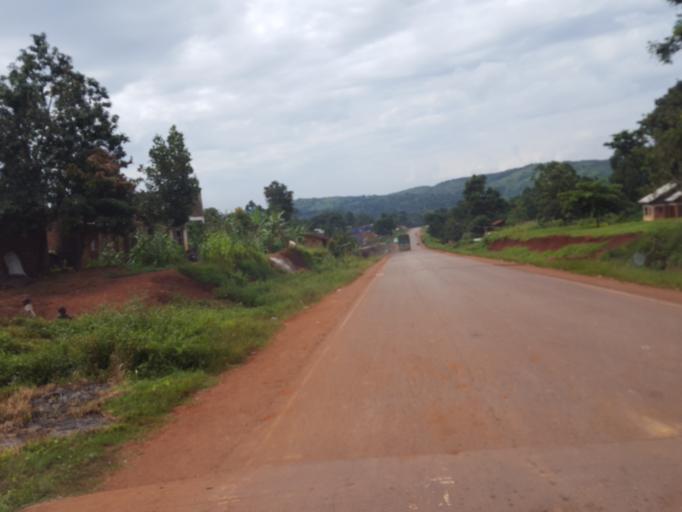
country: UG
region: Central Region
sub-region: Mityana District
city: Mityana
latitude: 0.6353
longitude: 32.1082
